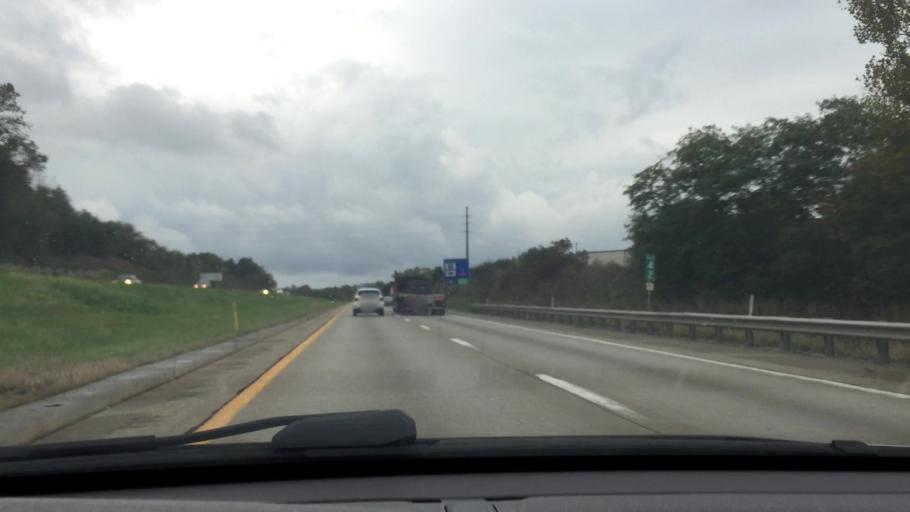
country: US
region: Pennsylvania
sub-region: Washington County
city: Houston
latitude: 40.2376
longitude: -80.2077
